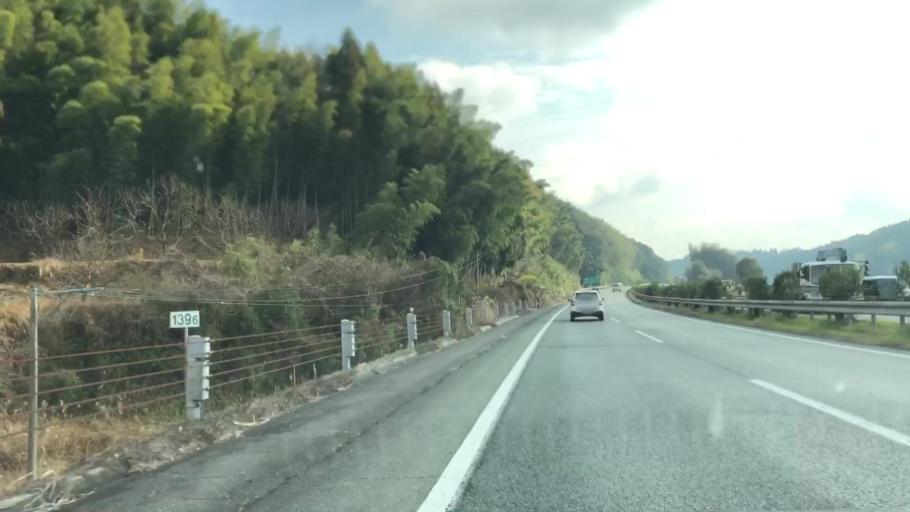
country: JP
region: Kumamoto
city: Yamaga
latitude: 33.0395
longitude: 130.5699
